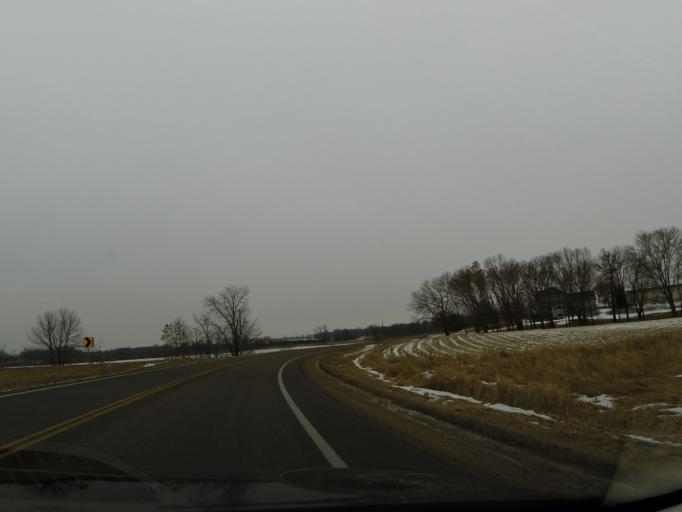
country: US
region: Minnesota
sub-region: Scott County
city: Prior Lake
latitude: 44.6303
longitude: -93.4830
